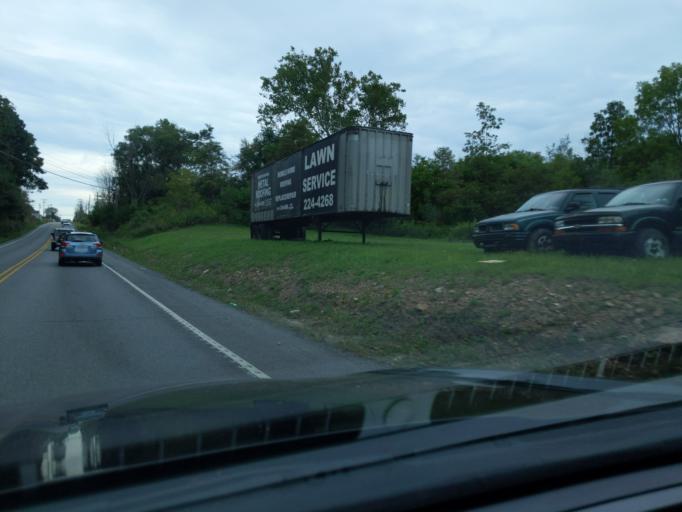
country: US
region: Pennsylvania
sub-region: Blair County
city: Duncansville
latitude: 40.4167
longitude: -78.4381
